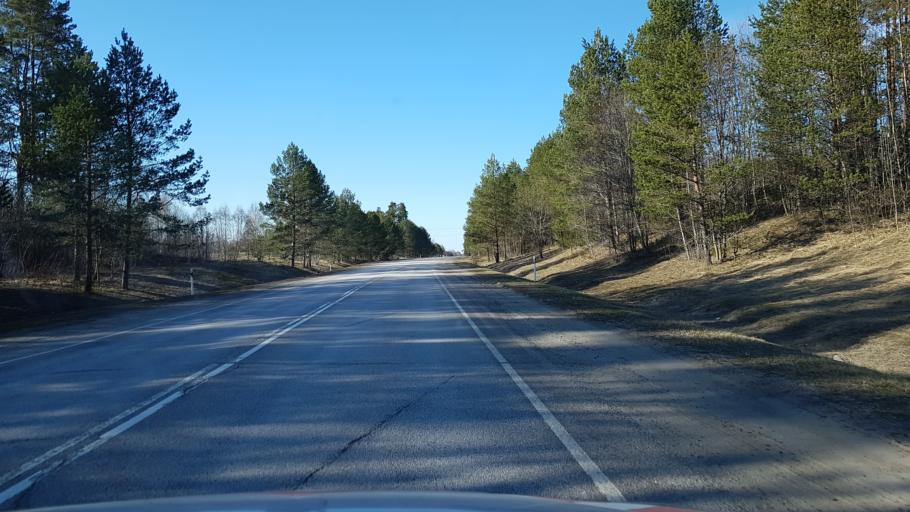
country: EE
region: Ida-Virumaa
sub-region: Johvi vald
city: Johvi
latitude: 59.1626
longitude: 27.3536
